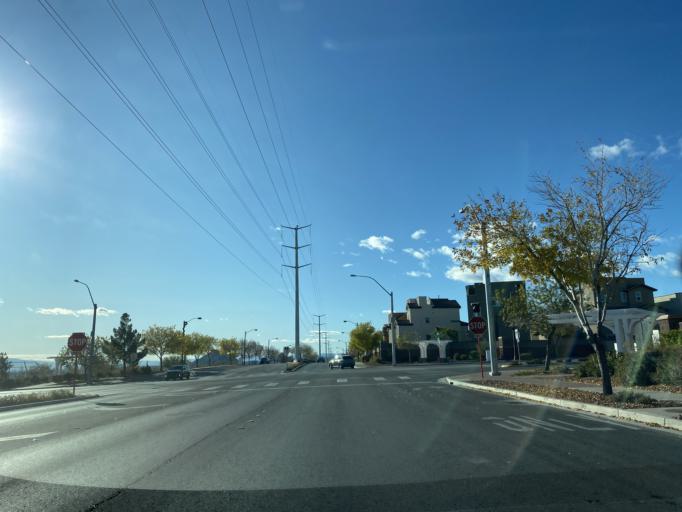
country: US
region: Nevada
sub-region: Clark County
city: Summerlin South
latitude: 36.2887
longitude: -115.3290
